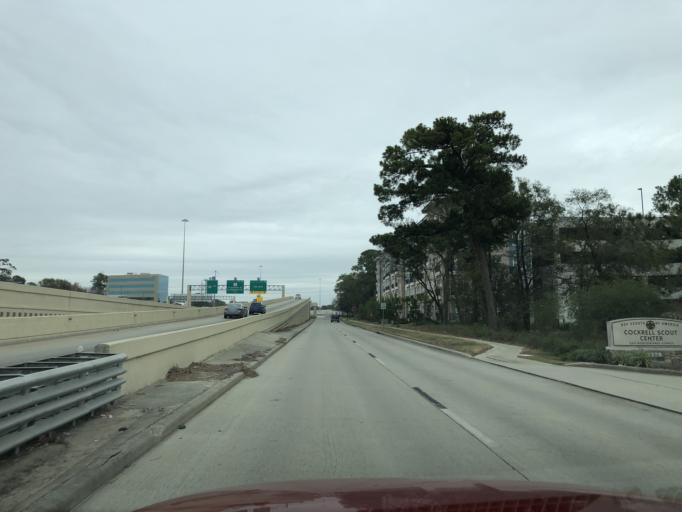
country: US
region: Texas
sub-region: Harris County
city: Spring Valley
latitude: 29.8096
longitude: -95.4384
